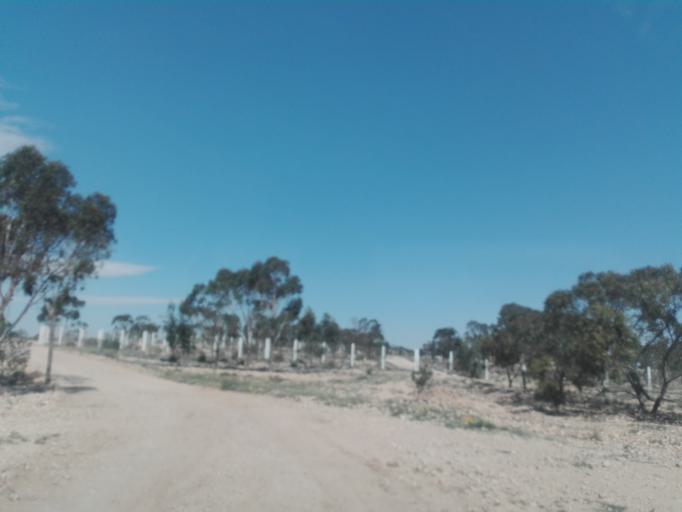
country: TN
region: Safaqis
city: Sfax
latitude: 34.7023
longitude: 10.5285
